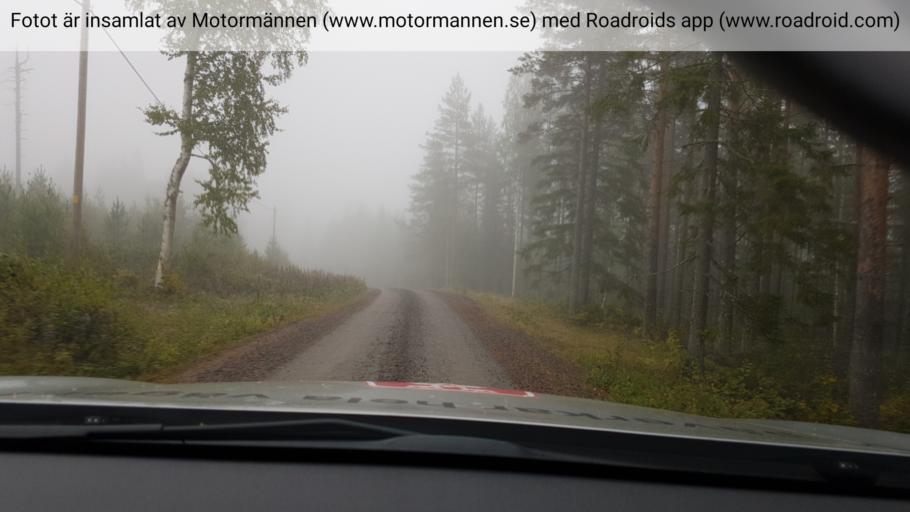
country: SE
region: Vaesterbotten
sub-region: Skelleftea Kommun
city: Burtraesk
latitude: 64.2947
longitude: 20.4008
